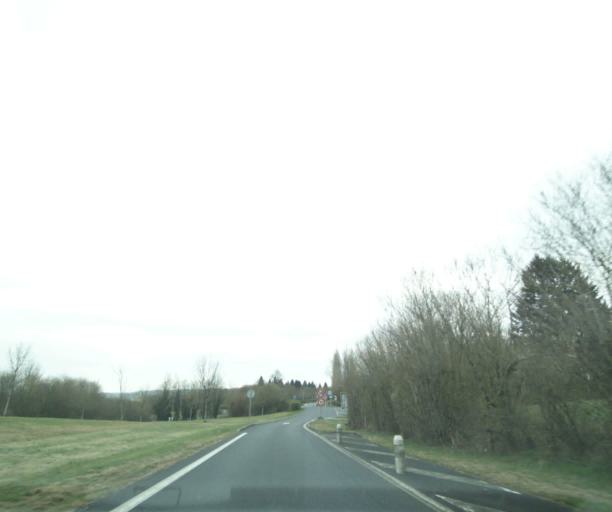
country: FR
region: Limousin
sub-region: Departement de la Correze
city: Vigeois
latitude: 45.3614
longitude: 1.5697
